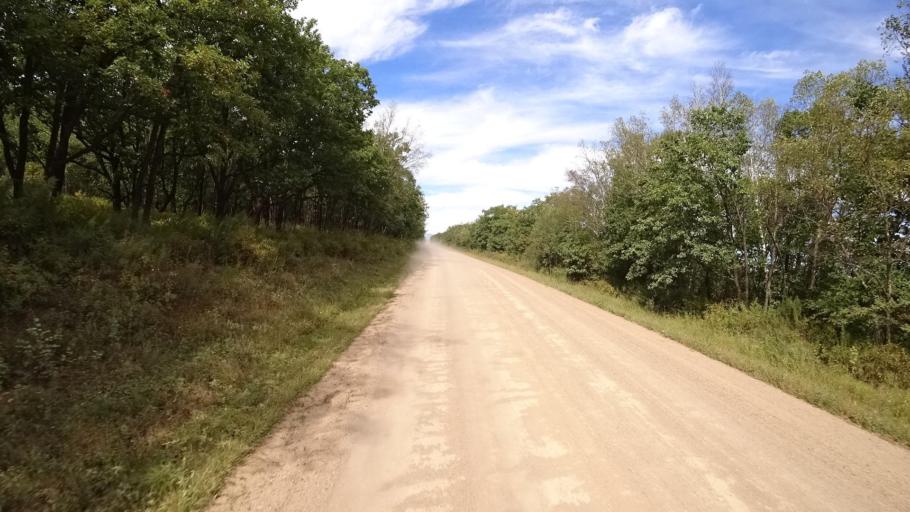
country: RU
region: Primorskiy
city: Yakovlevka
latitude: 44.5980
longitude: 133.6058
